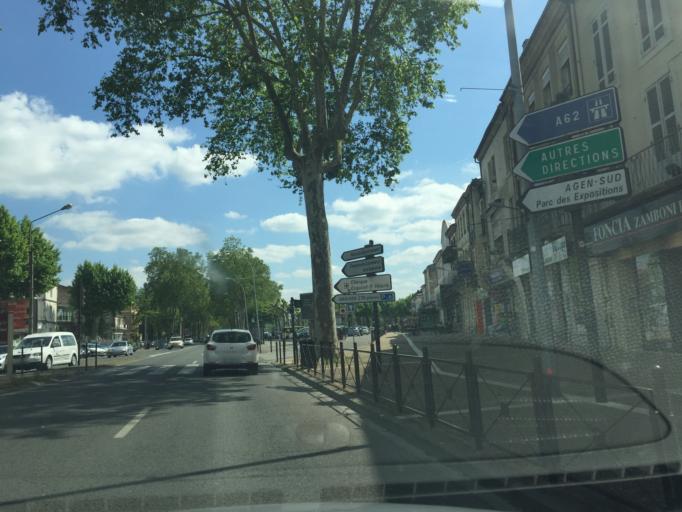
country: FR
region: Aquitaine
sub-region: Departement du Lot-et-Garonne
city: Le Passage
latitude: 44.2042
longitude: 0.6117
